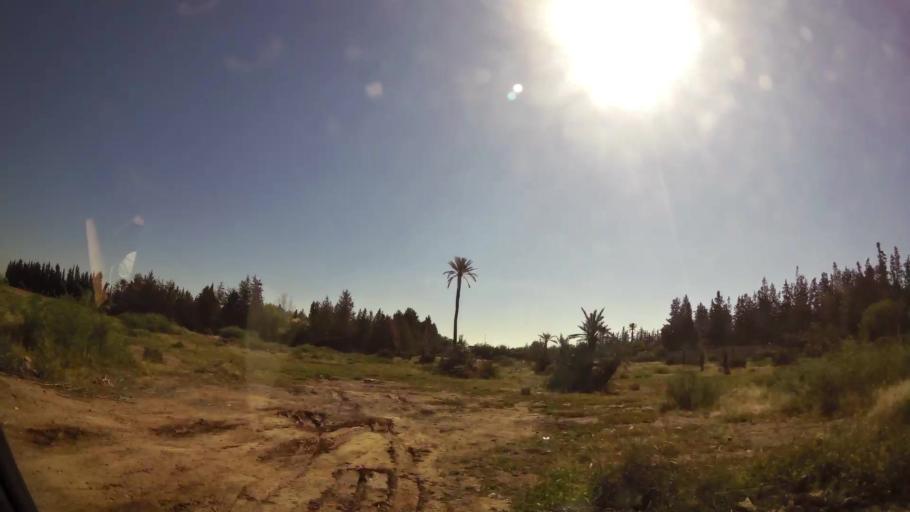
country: MA
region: Marrakech-Tensift-Al Haouz
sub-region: Marrakech
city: Marrakesh
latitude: 31.6632
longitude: -7.9400
